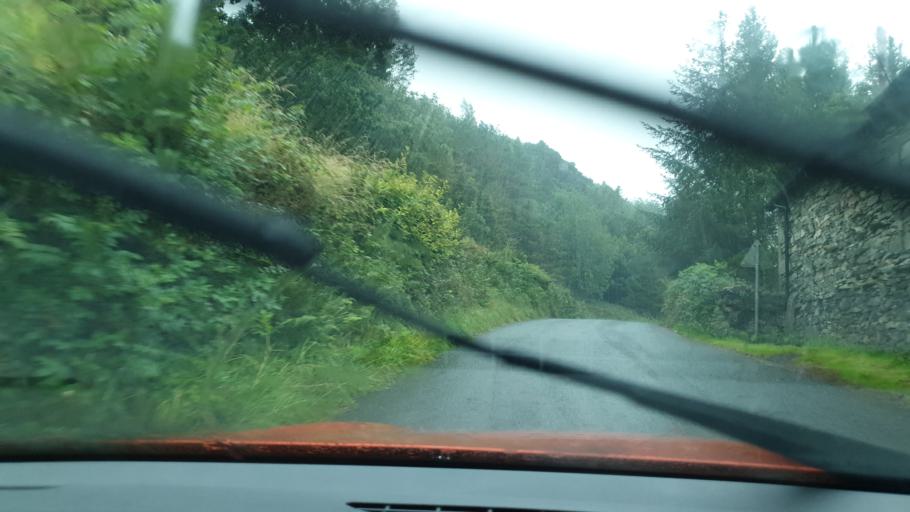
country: GB
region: England
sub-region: Cumbria
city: Millom
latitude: 54.3023
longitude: -3.2284
